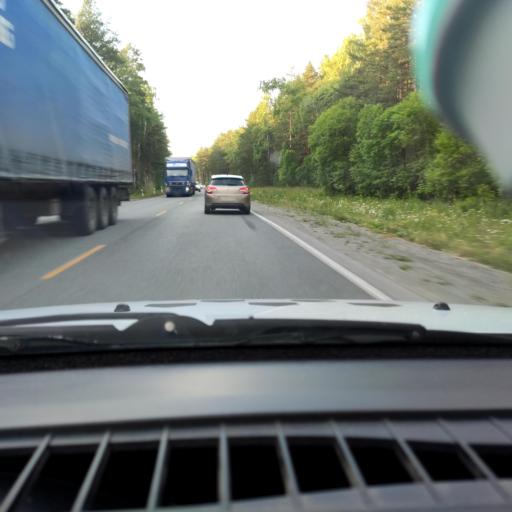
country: RU
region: Chelyabinsk
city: Turgoyak
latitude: 55.2801
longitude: 60.1971
